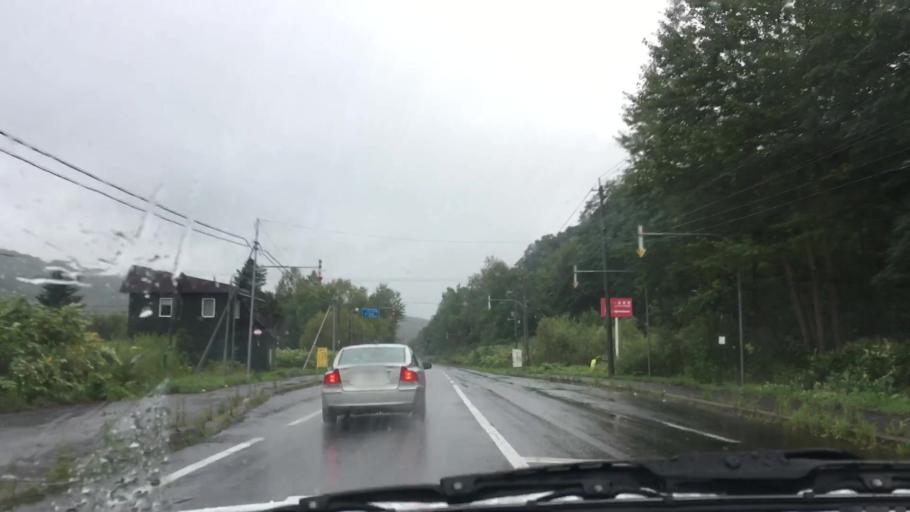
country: JP
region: Hokkaido
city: Niseko Town
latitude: 42.8075
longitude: 140.9983
